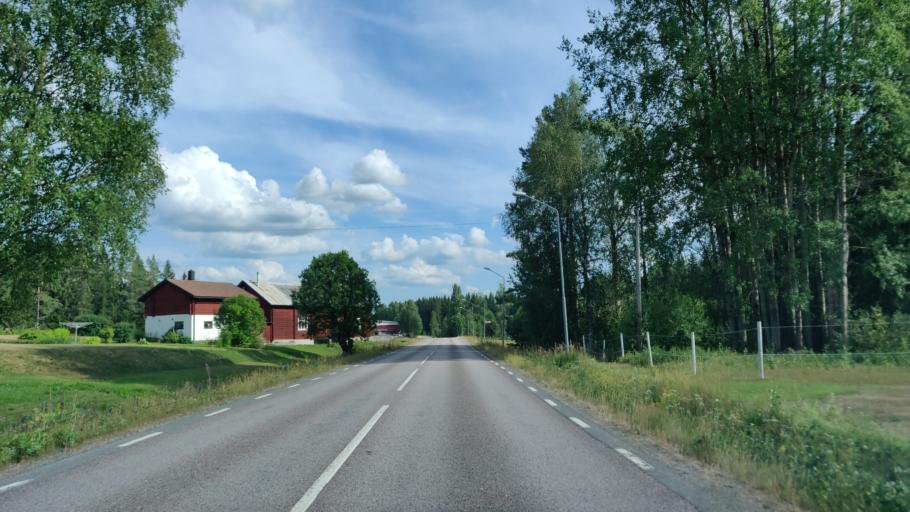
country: SE
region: Vaermland
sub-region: Hagfors Kommun
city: Hagfors
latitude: 60.0715
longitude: 13.6308
